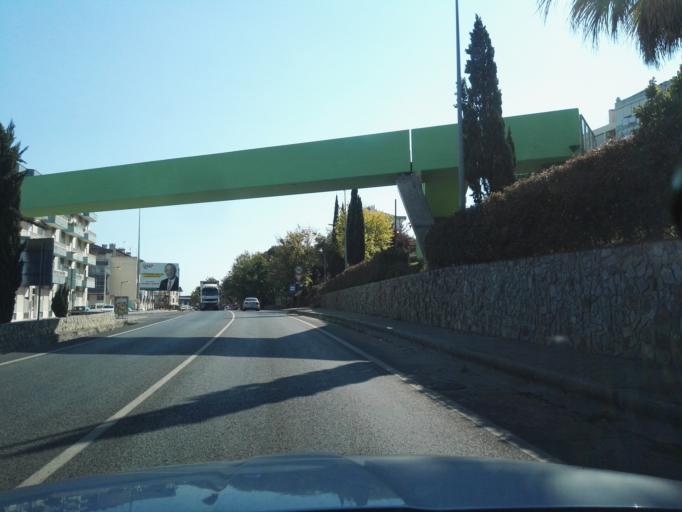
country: PT
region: Lisbon
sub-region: Vila Franca de Xira
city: Vialonga
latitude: 38.8730
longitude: -9.0546
